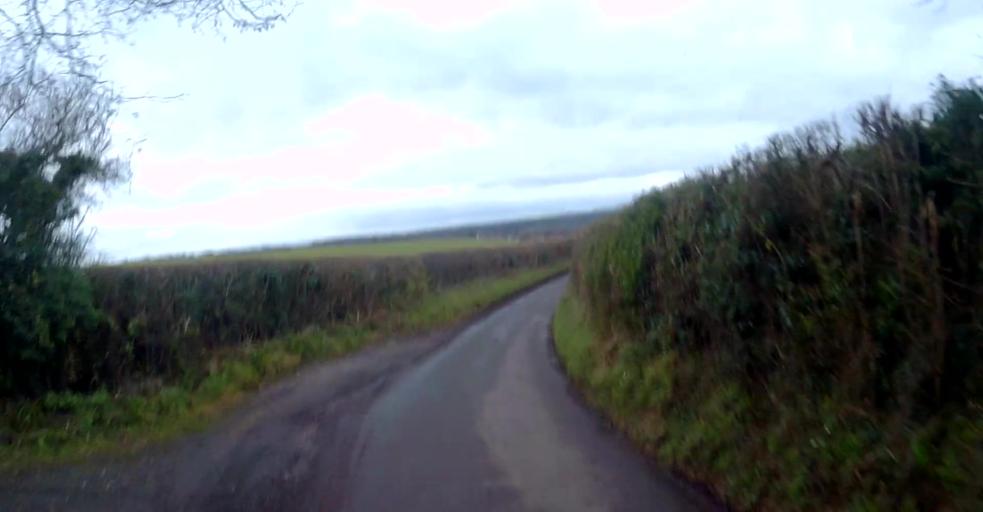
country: GB
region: England
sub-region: Hampshire
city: Overton
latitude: 51.2343
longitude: -1.2505
